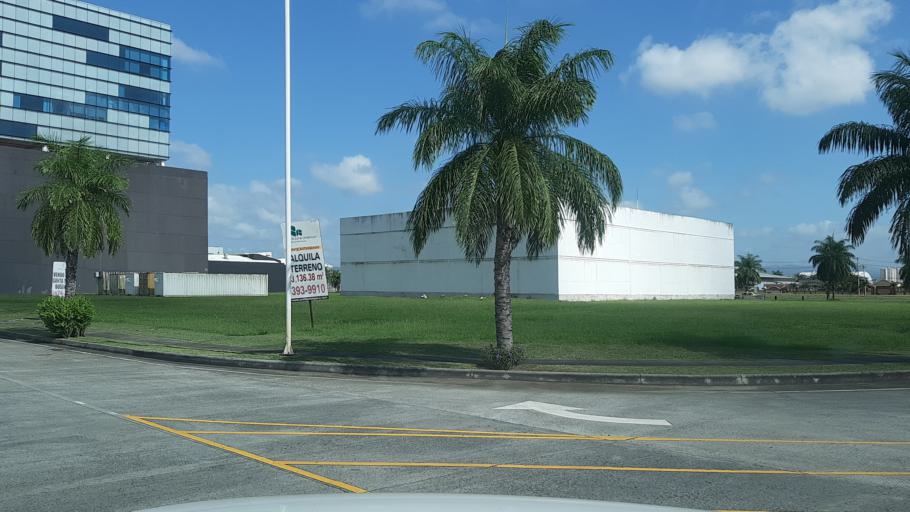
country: PA
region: Panama
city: San Miguelito
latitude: 9.0297
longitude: -79.4581
